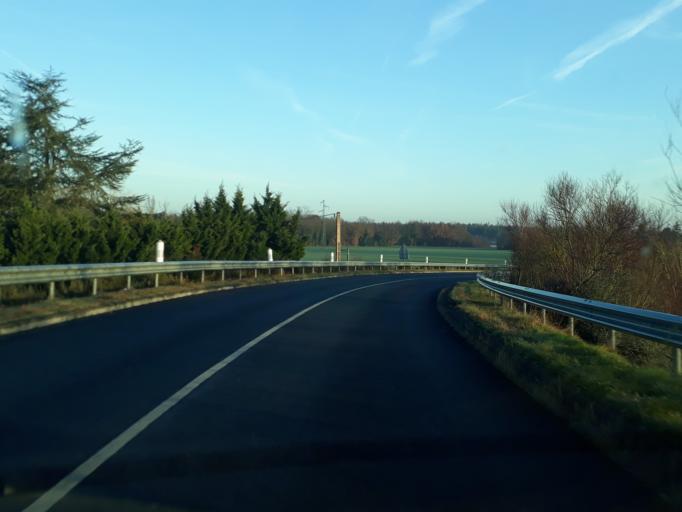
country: FR
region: Midi-Pyrenees
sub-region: Departement de la Haute-Garonne
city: Marquefave
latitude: 43.3277
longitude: 1.2300
